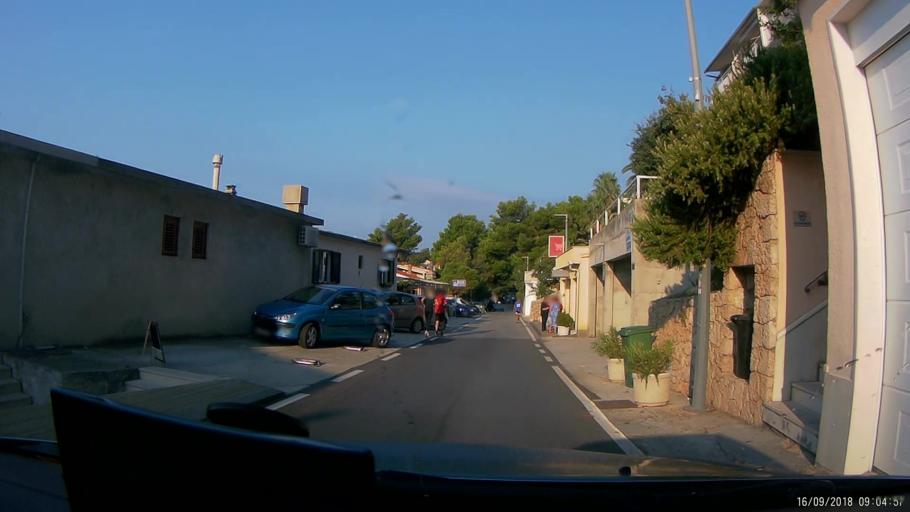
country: HR
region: Splitsko-Dalmatinska
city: Donja Brela
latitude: 43.3684
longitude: 16.9314
